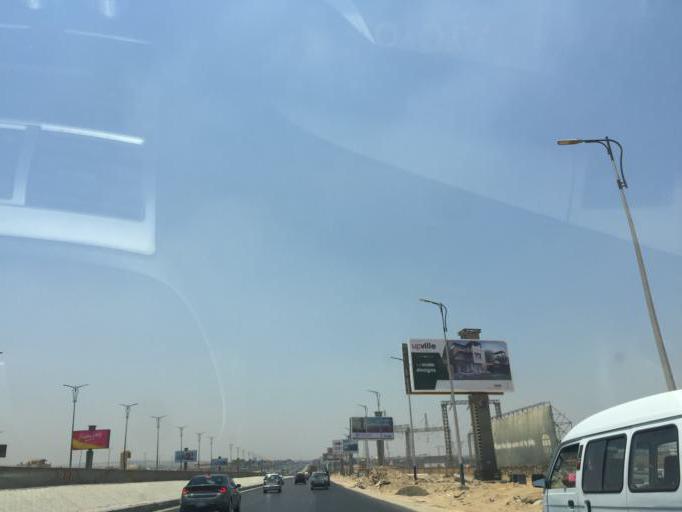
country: EG
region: Al Jizah
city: Awsim
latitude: 30.0491
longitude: 31.0496
